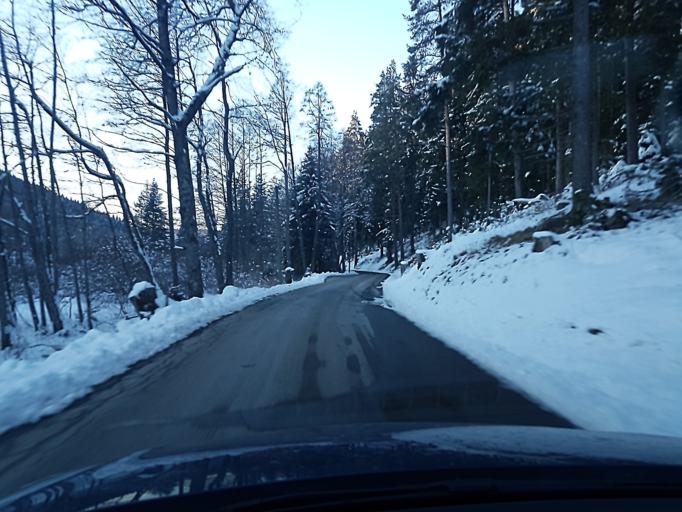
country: DE
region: Baden-Wuerttemberg
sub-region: Freiburg Region
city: Monchweiler
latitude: 48.0940
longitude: 8.4011
